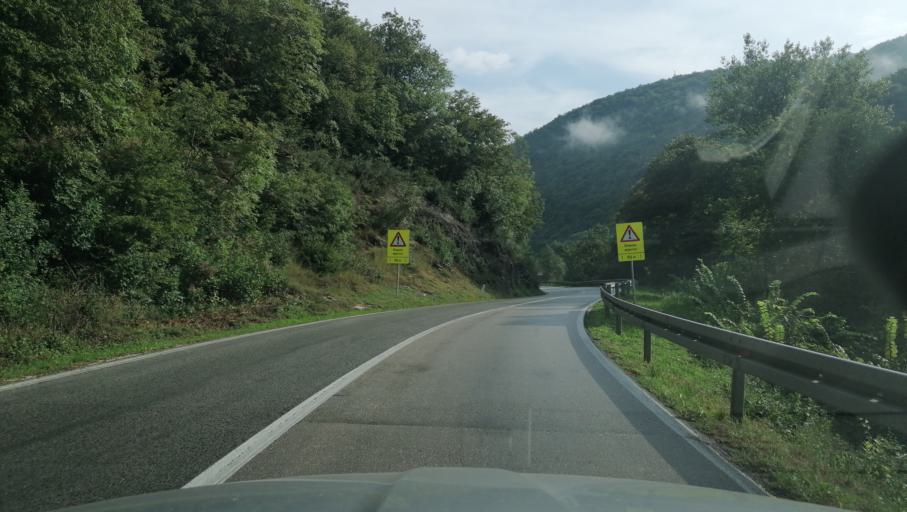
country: BA
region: Republika Srpska
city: Hiseti
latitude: 44.6631
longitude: 17.1426
